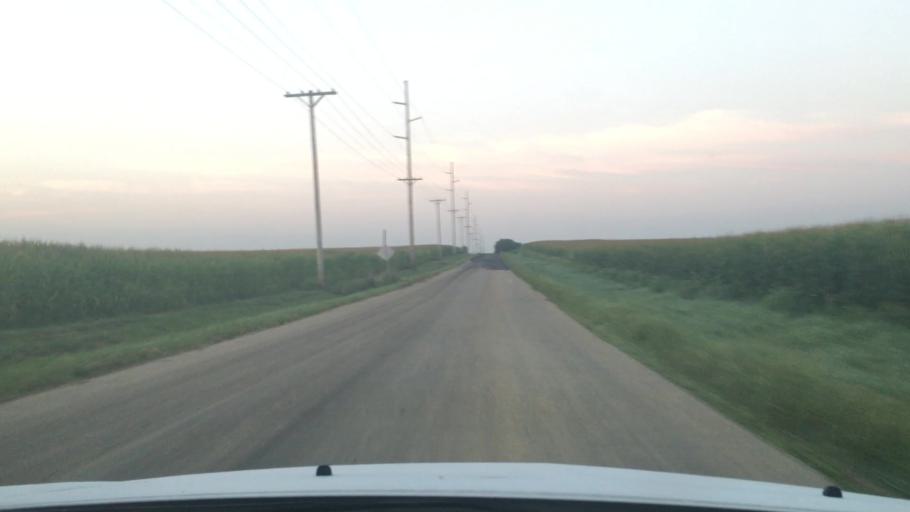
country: US
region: Illinois
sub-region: Ogle County
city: Rochelle
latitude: 41.9195
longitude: -89.0001
